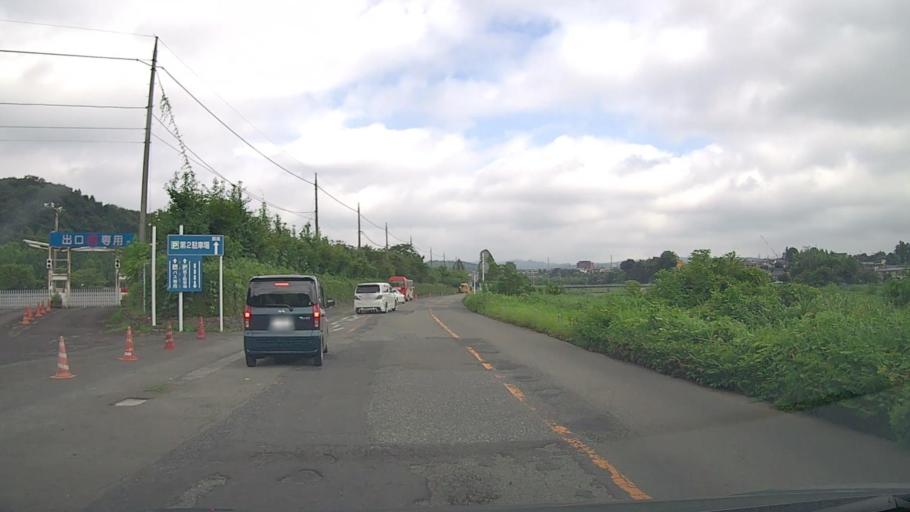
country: JP
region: Tokyo
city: Itsukaichi
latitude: 35.7168
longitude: 139.2649
